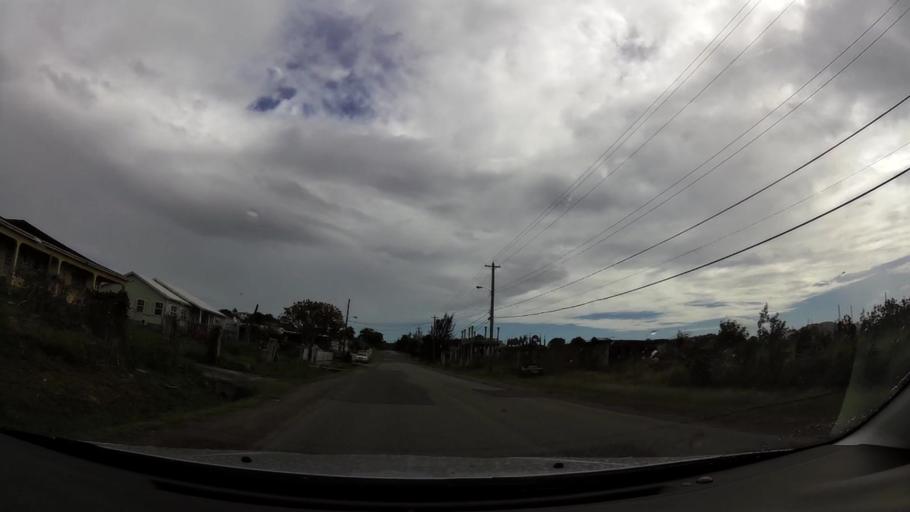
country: AG
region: Saint John
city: Saint John's
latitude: 17.1029
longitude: -61.8308
